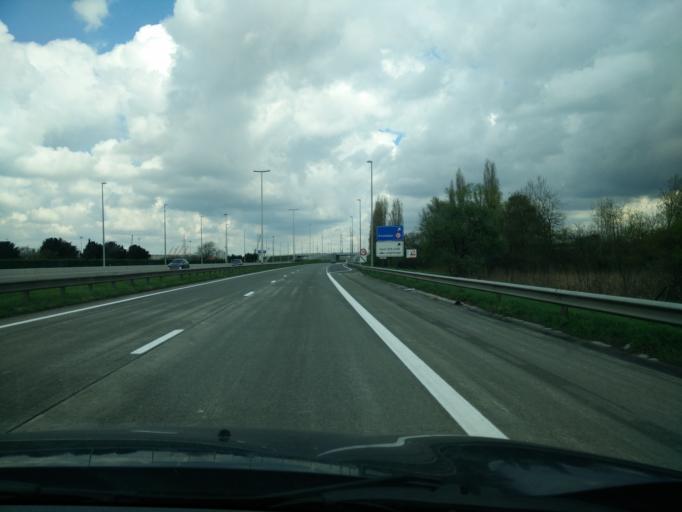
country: BE
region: Flanders
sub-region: Provincie Oost-Vlaanderen
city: Evergem
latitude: 51.0998
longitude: 3.7571
